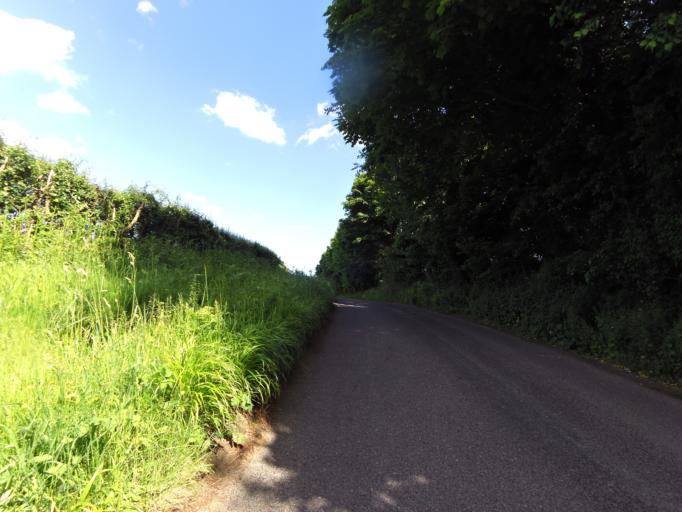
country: GB
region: England
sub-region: Suffolk
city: Shotley Gate
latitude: 52.0077
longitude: 1.2455
